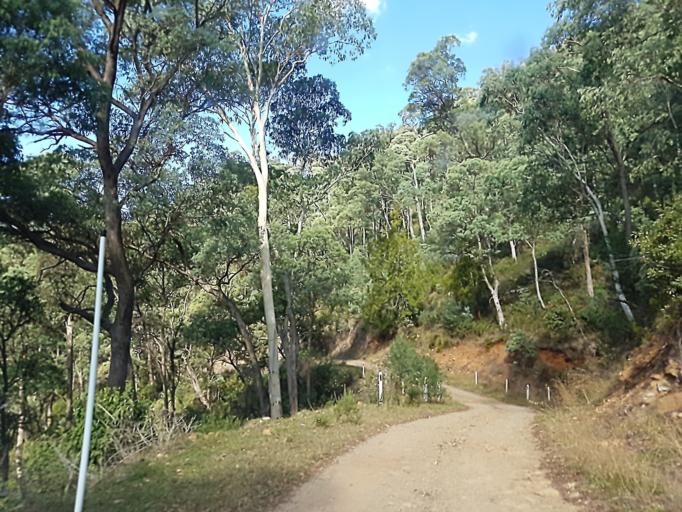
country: AU
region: Victoria
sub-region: Alpine
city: Mount Beauty
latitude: -36.9227
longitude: 147.0367
